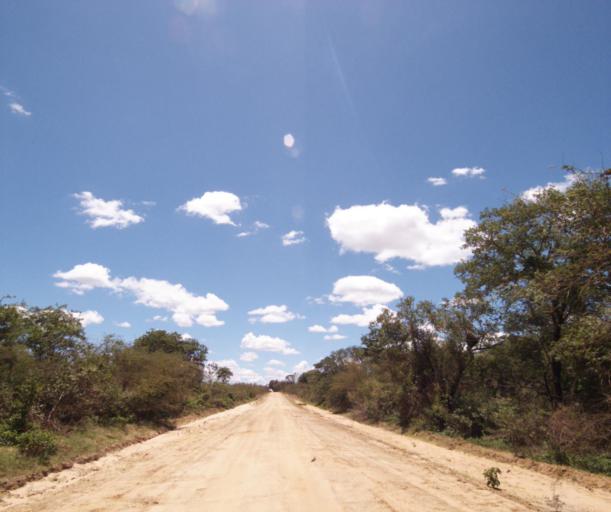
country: BR
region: Bahia
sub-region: Carinhanha
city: Carinhanha
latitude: -14.2100
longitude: -43.9822
